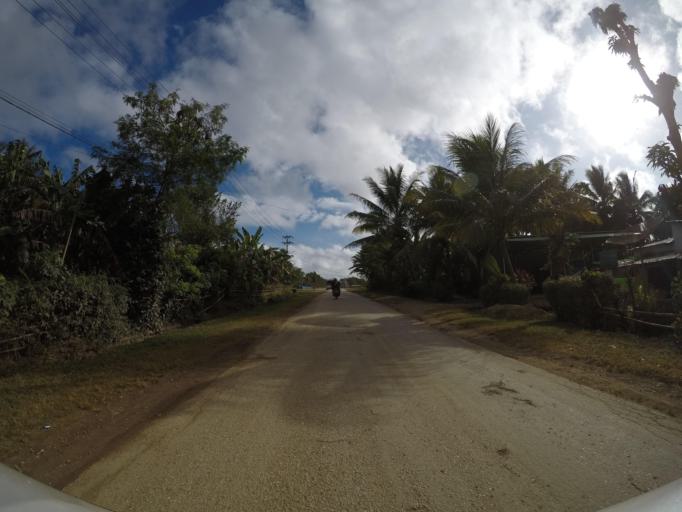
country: TL
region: Lautem
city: Lospalos
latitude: -8.4979
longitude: 126.9913
